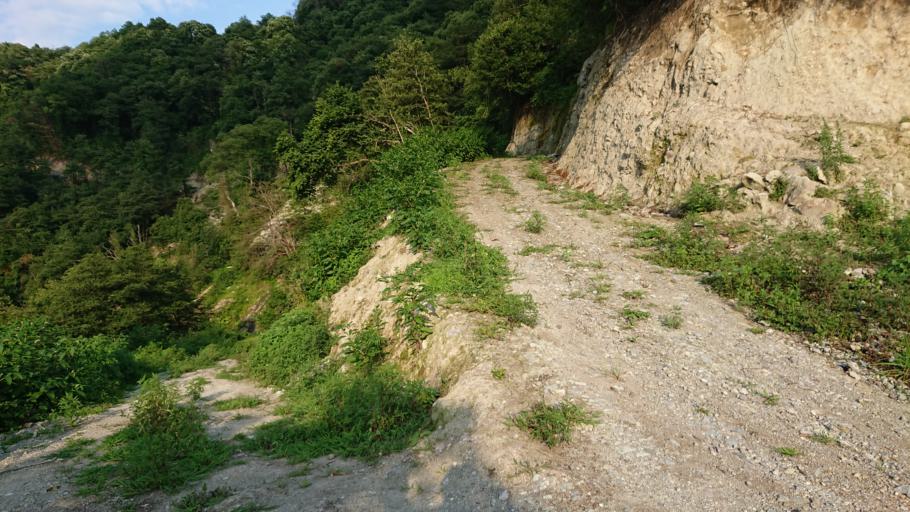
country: TR
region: Rize
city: Rize
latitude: 40.9879
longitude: 40.5019
